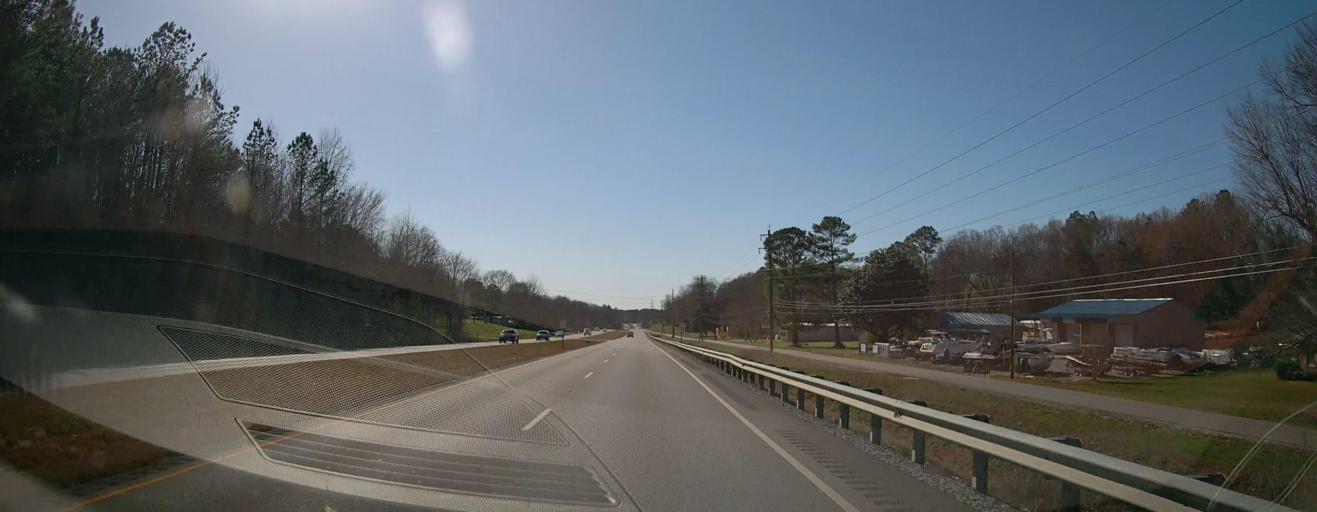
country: US
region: Alabama
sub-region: Lauderdale County
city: Killen
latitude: 34.8598
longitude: -87.5072
